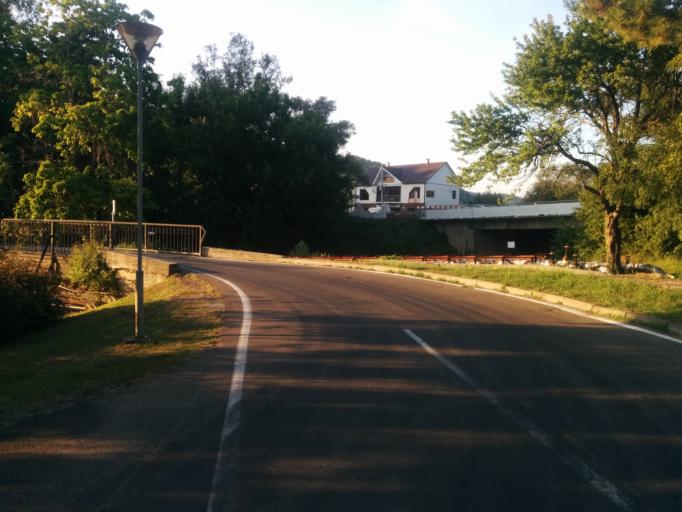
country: RU
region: Krasnodarskiy
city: Novomikhaylovskiy
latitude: 44.2592
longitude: 38.8223
